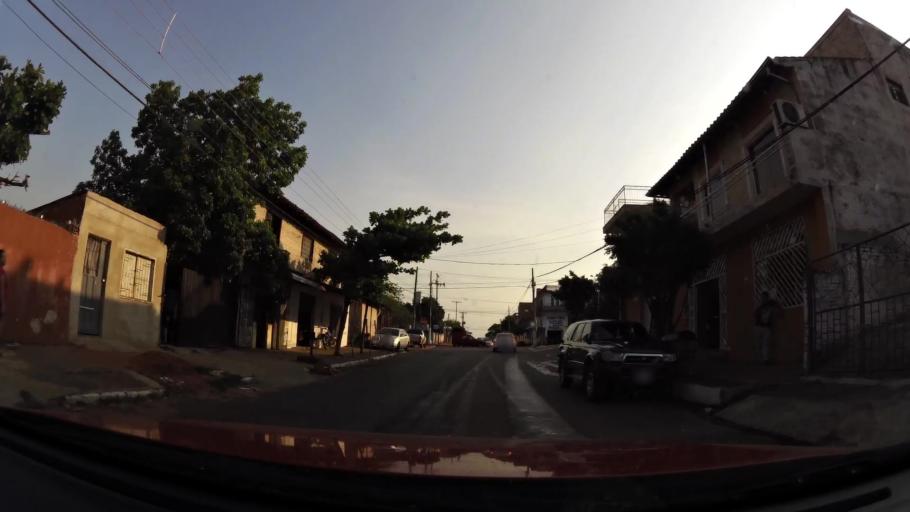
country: PY
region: Central
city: Lambare
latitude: -25.3561
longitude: -57.5982
